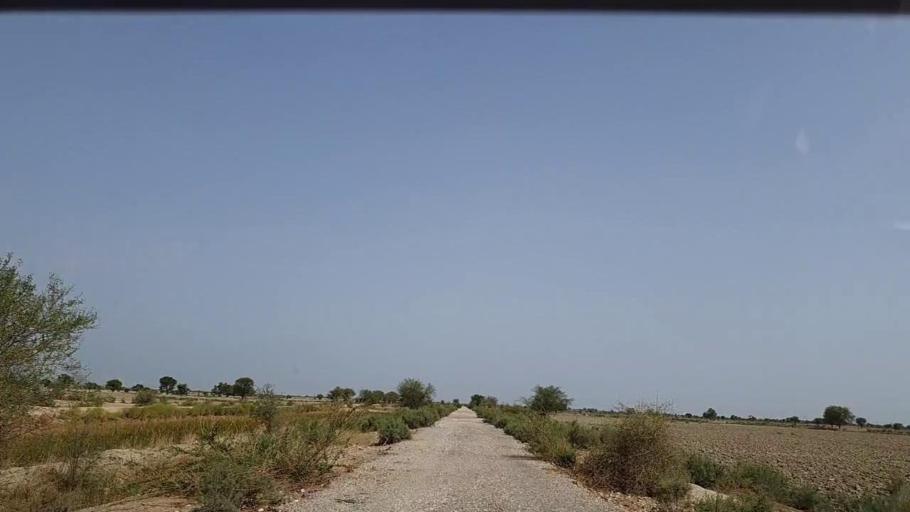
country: PK
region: Sindh
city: Johi
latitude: 26.7526
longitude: 67.6696
